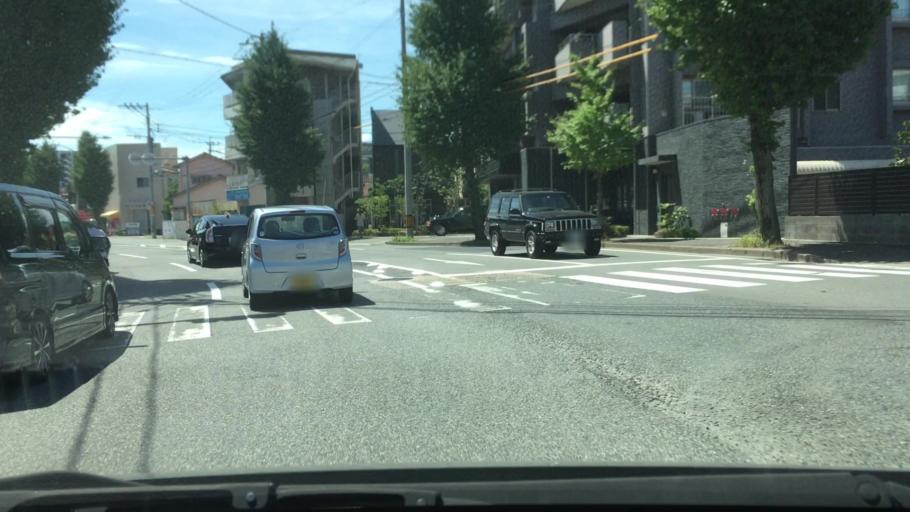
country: JP
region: Fukuoka
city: Fukuoka-shi
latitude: 33.5735
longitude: 130.4216
